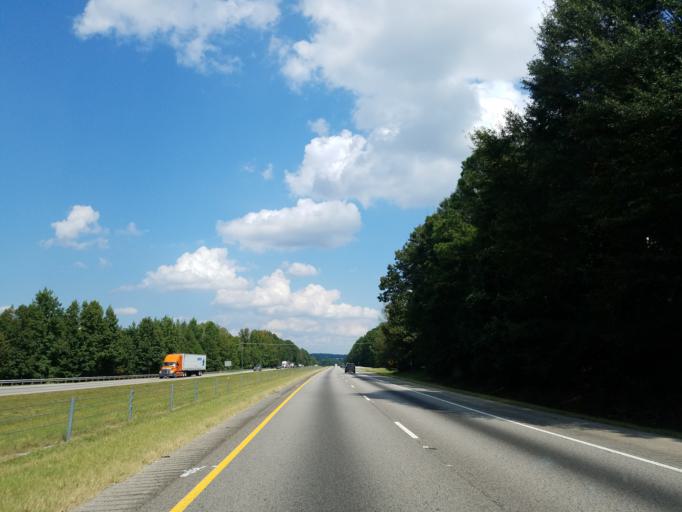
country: US
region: Georgia
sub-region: Jackson County
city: Hoschton
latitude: 34.0971
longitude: -83.8113
